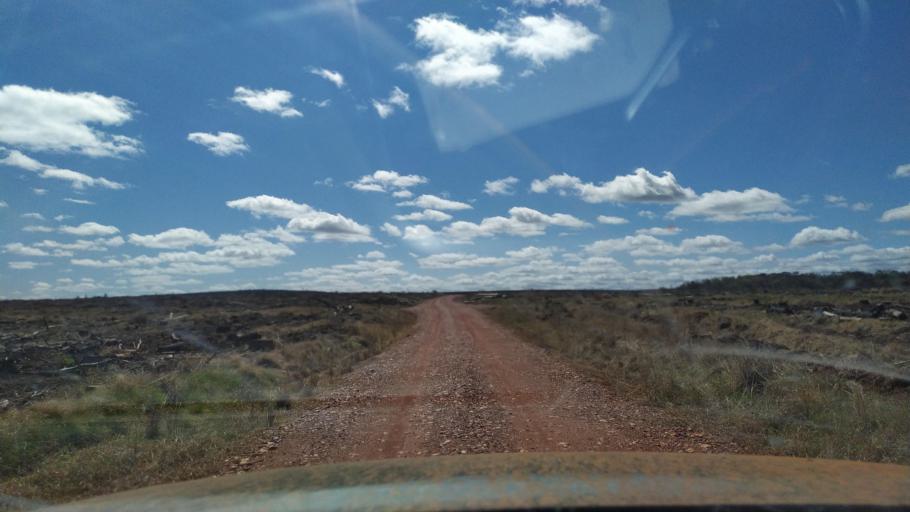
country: AR
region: Corrientes
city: Gobernador Ingeniero Valentin Virasoro
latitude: -28.2969
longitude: -56.0534
